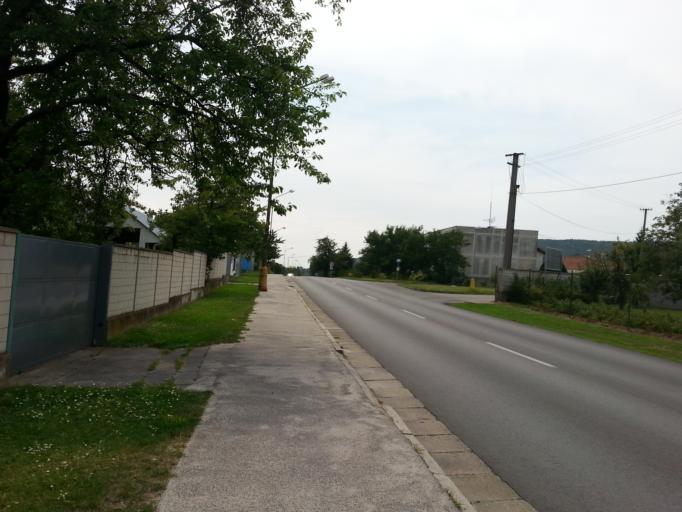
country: SK
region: Trenciansky
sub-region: Okres Nove Mesto nad Vahom
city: Nove Mesto nad Vahom
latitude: 48.7486
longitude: 17.8247
